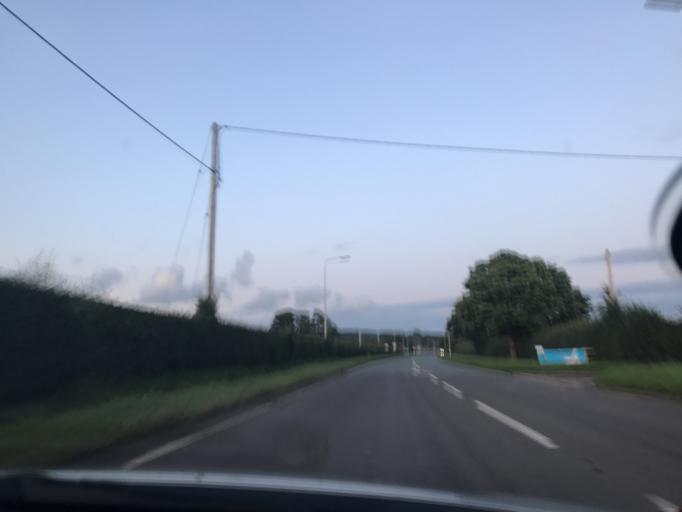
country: GB
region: England
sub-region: Cheshire West and Chester
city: Tarvin
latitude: 53.2084
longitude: -2.7429
